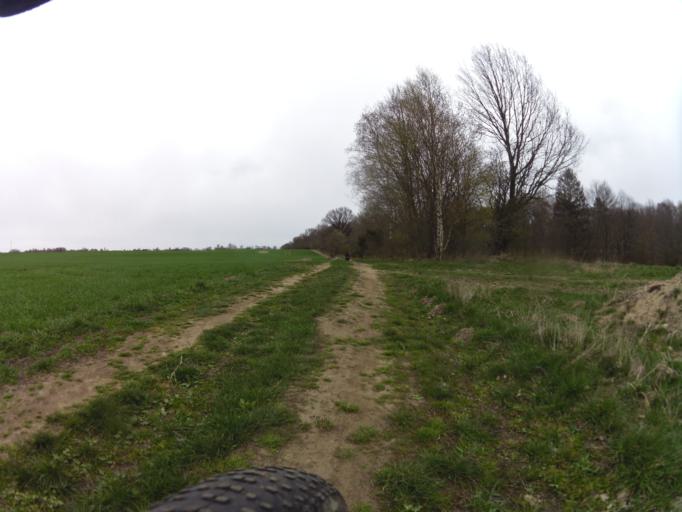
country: PL
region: West Pomeranian Voivodeship
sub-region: Powiat koszalinski
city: Polanow
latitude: 54.1223
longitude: 16.6195
